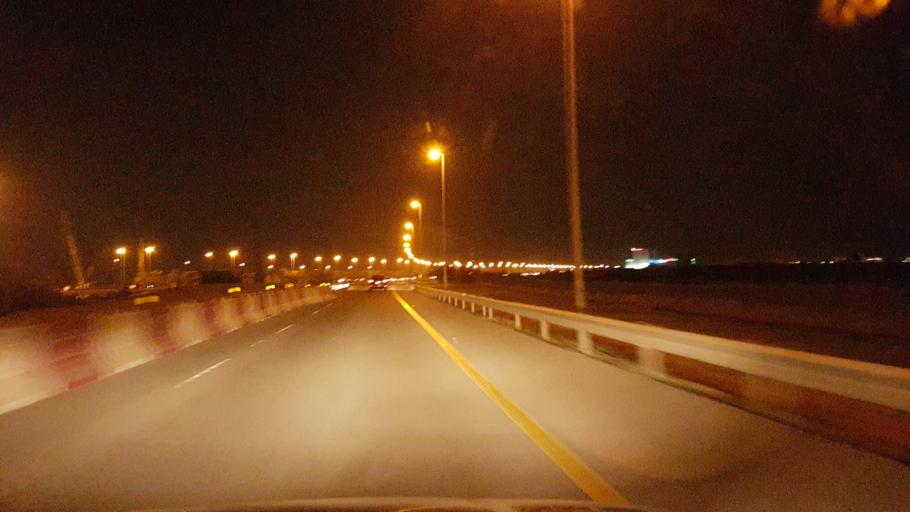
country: BH
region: Northern
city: Madinat `Isa
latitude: 26.1862
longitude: 50.5010
